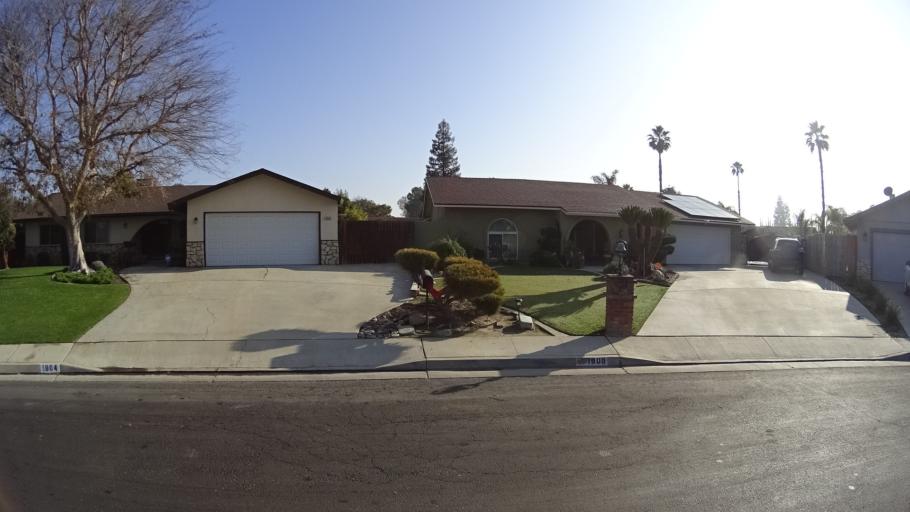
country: US
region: California
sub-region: Kern County
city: Bakersfield
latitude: 35.3375
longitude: -119.0670
